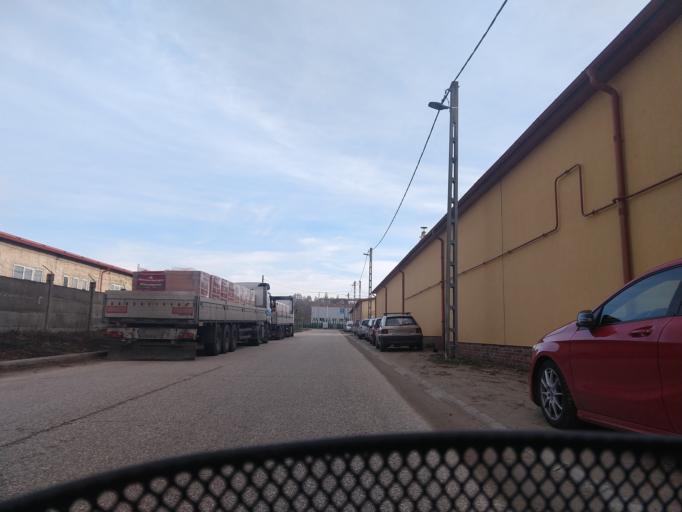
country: HU
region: Pest
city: Orbottyan
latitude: 47.6668
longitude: 19.2763
